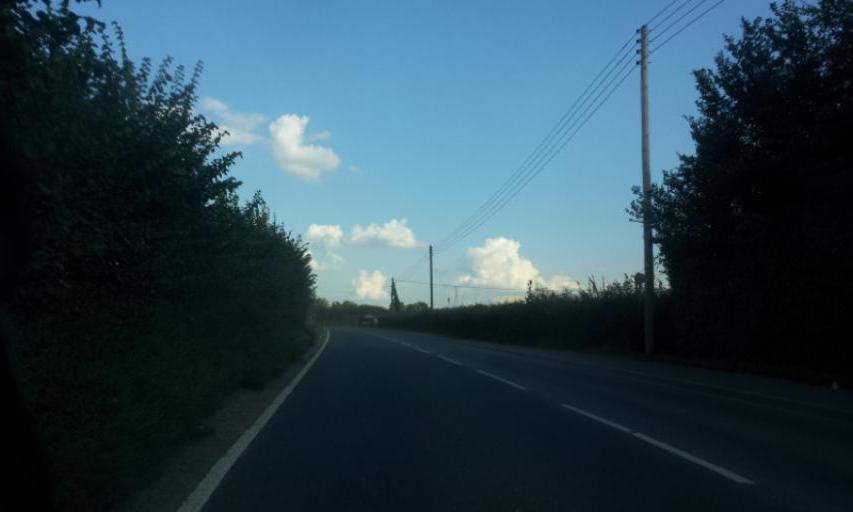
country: GB
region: England
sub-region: Kent
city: Longfield
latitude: 51.4037
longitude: 0.2858
